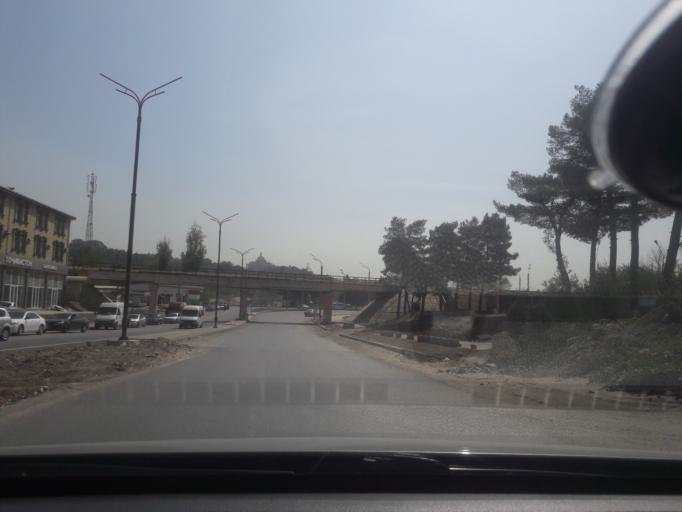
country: TJ
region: Dushanbe
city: Dushanbe
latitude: 38.6036
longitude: 68.7738
